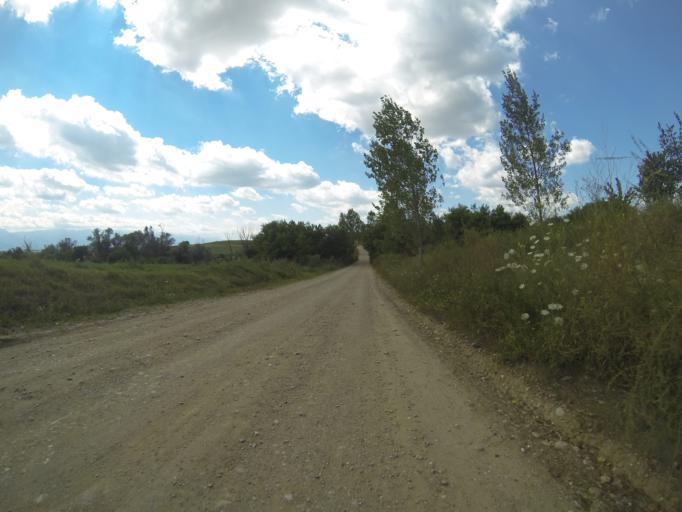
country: RO
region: Brasov
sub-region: Comuna Mandra
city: Mandra
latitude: 45.8450
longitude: 25.0299
